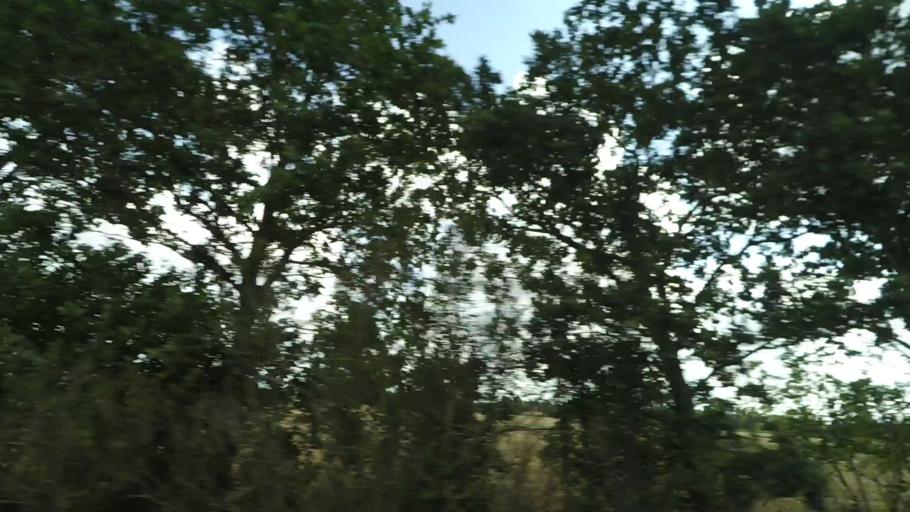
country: DK
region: Central Jutland
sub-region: Norddjurs Kommune
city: Auning
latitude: 56.5012
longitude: 10.4301
